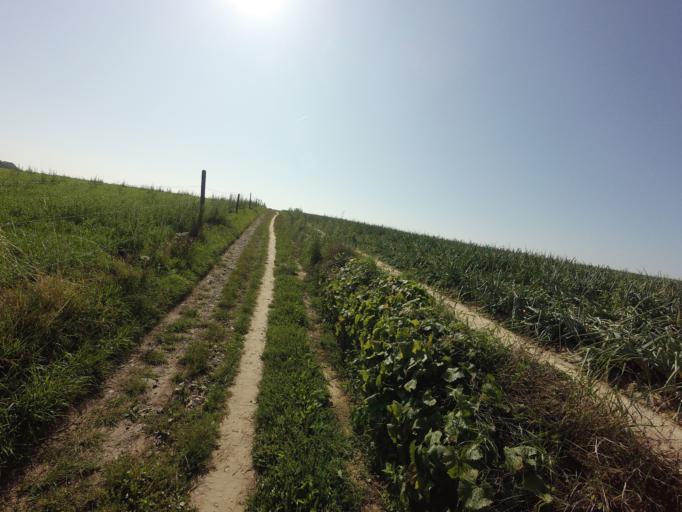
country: NL
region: Limburg
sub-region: Valkenburg aan de Geul
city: Schin op Geul
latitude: 50.8251
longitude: 5.8688
